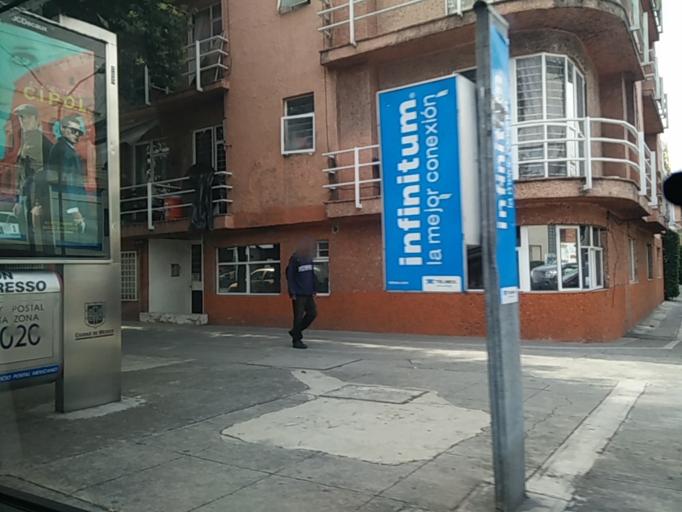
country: MX
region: Mexico City
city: Benito Juarez
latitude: 19.3960
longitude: -99.1589
